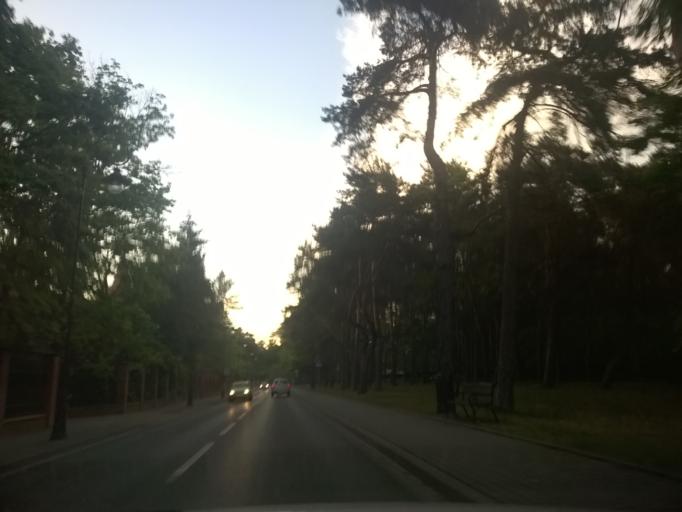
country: PL
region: Masovian Voivodeship
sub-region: Powiat piaseczynski
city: Konstancin-Jeziorna
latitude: 52.0817
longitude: 21.1190
